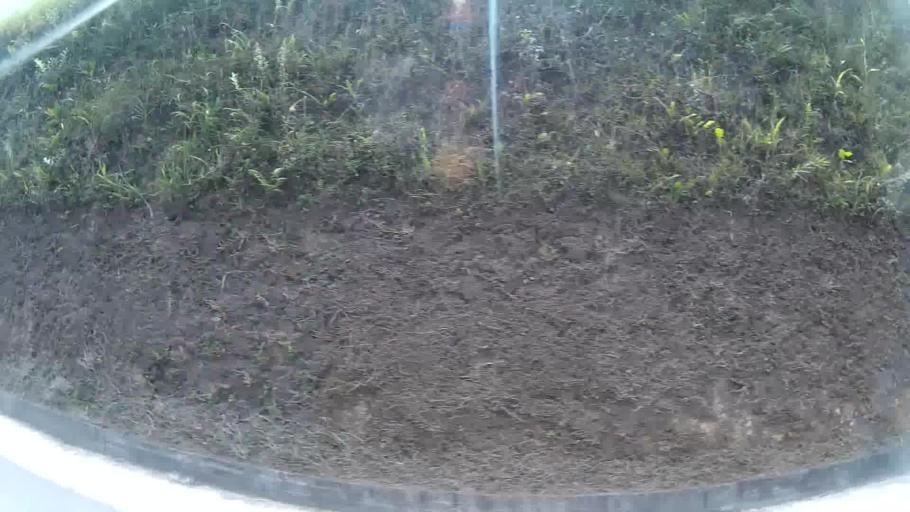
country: CO
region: Risaralda
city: Pereira
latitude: 4.7956
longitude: -75.7507
